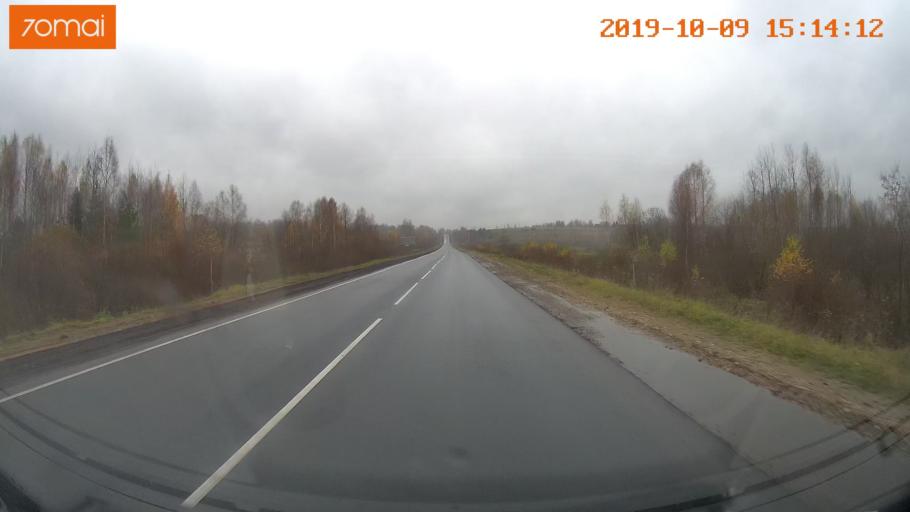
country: RU
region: Kostroma
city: Susanino
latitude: 58.1373
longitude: 41.6041
